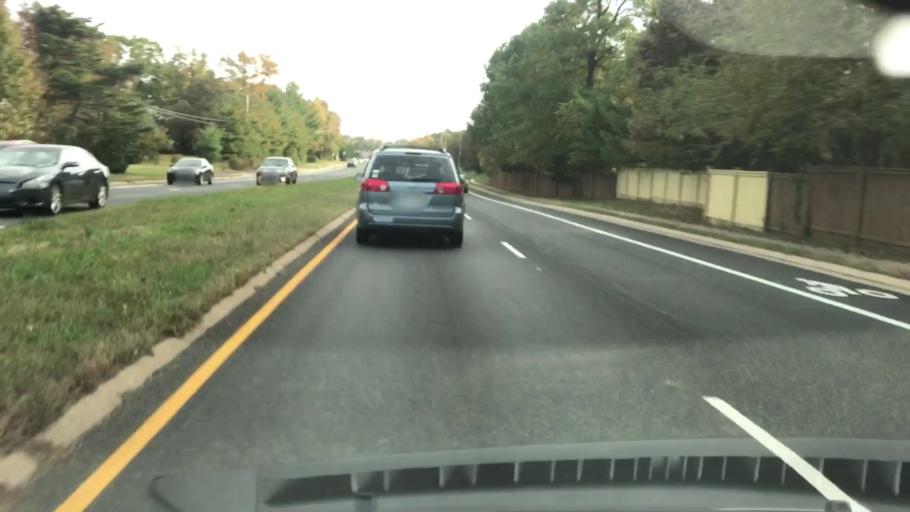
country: US
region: Virginia
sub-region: Fairfax County
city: Newington
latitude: 38.7477
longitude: -77.1674
